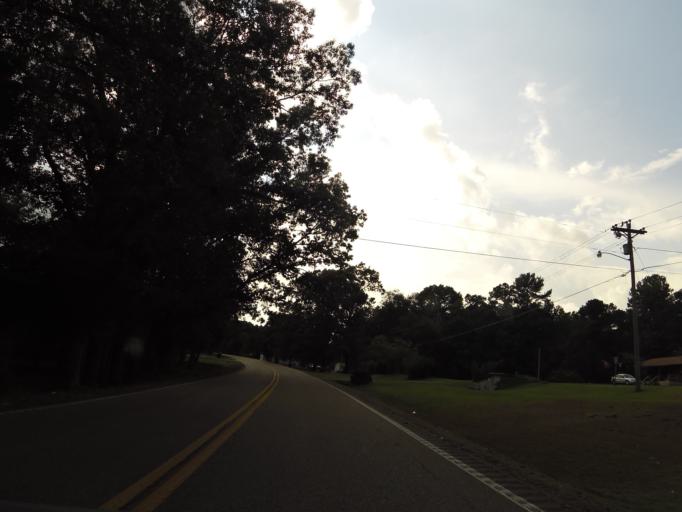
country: US
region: Mississippi
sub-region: Alcorn County
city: Farmington
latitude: 35.0632
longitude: -88.3982
